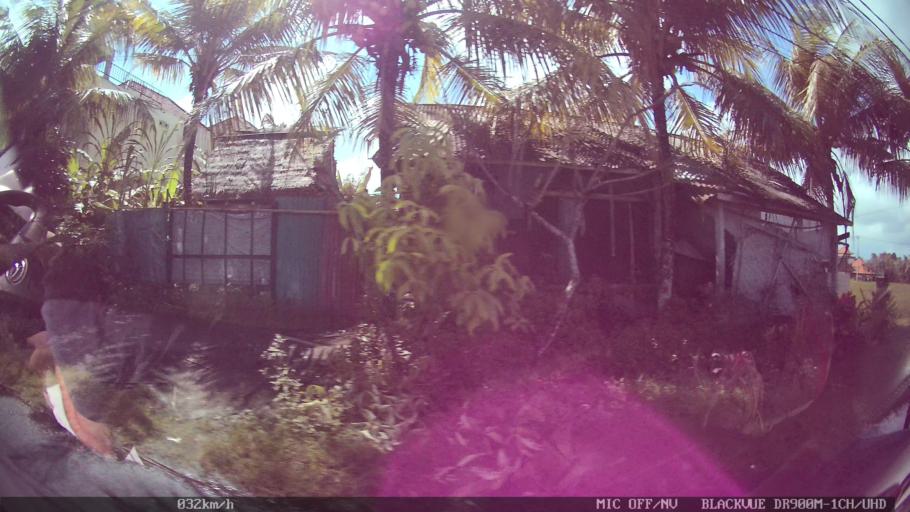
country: ID
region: Bali
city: Banjar Tebongkang
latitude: -8.5512
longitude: 115.2749
